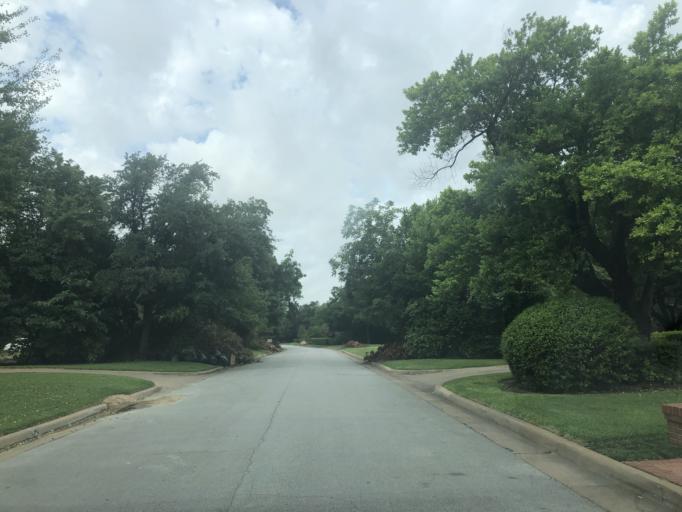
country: US
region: Texas
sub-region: Dallas County
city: University Park
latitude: 32.8623
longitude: -96.8228
